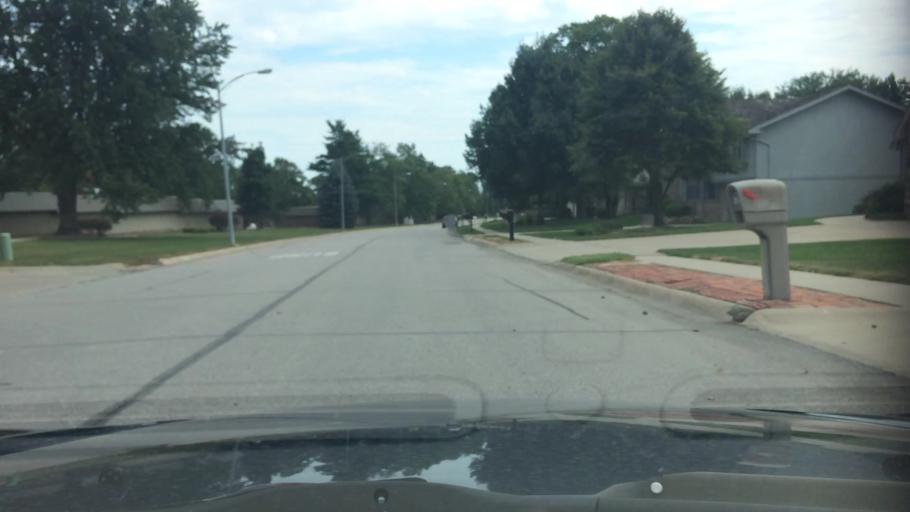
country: US
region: Nebraska
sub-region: Douglas County
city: Ralston
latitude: 41.1949
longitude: -96.0679
